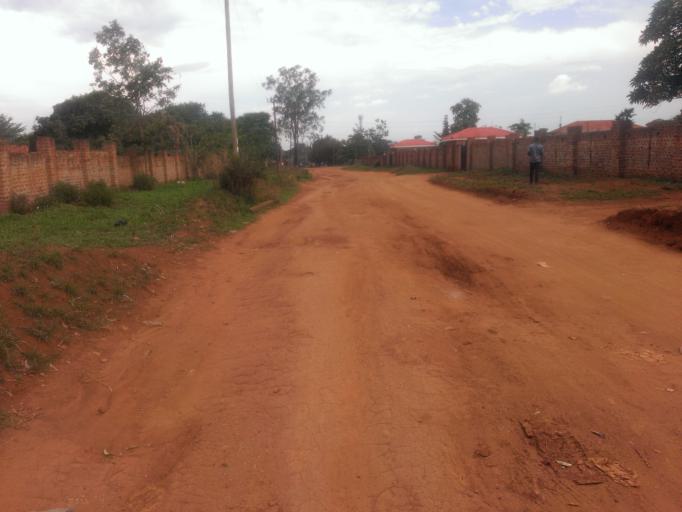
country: UG
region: Northern Region
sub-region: Gulu District
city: Gulu
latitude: 2.7817
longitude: 32.3029
